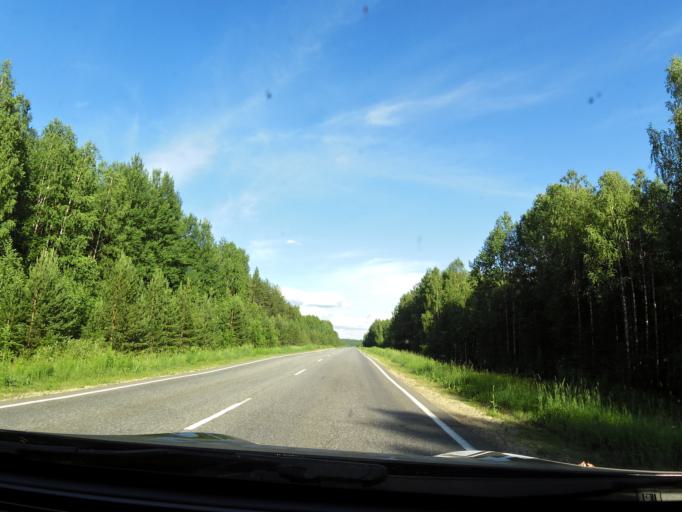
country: RU
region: Kirov
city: Chernaya Kholunitsa
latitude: 58.8289
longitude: 51.7683
